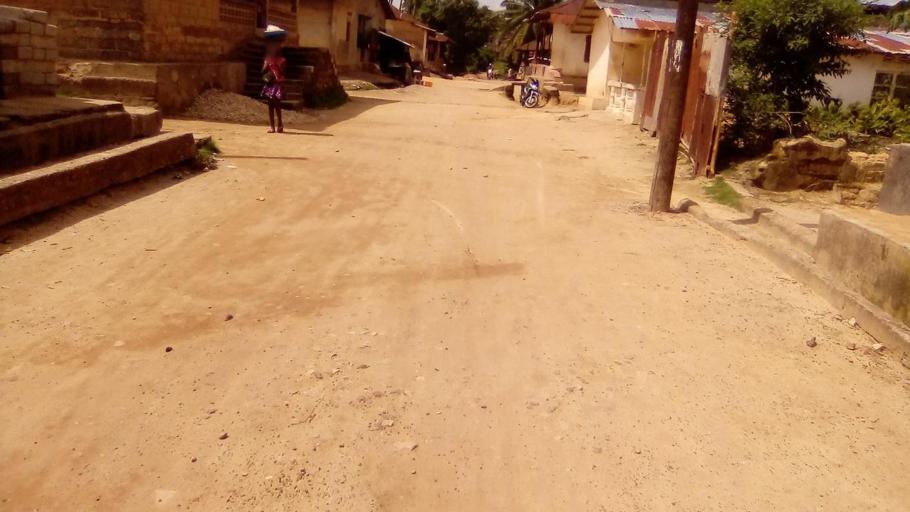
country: SL
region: Southern Province
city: Bo
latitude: 7.9662
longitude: -11.7335
